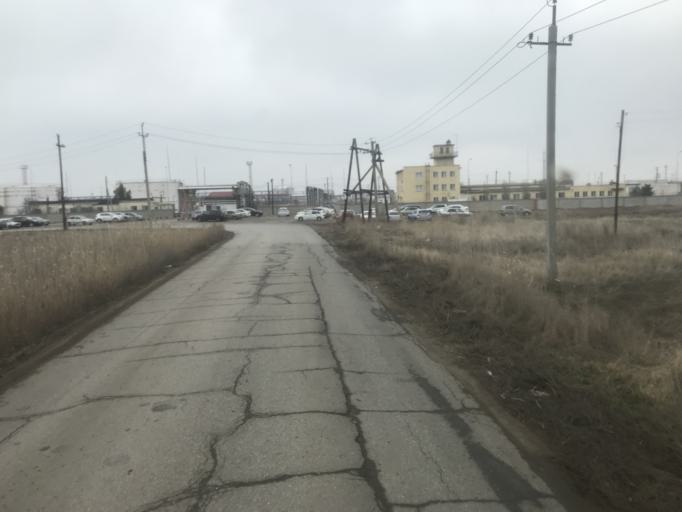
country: RU
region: Volgograd
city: Svetlyy Yar
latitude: 48.5032
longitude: 44.6461
